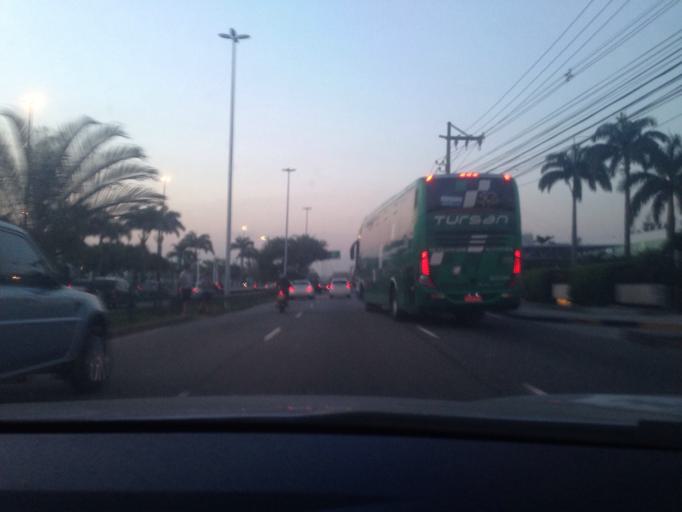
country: BR
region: Rio de Janeiro
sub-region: Rio De Janeiro
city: Rio de Janeiro
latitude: -22.9937
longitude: -43.3655
